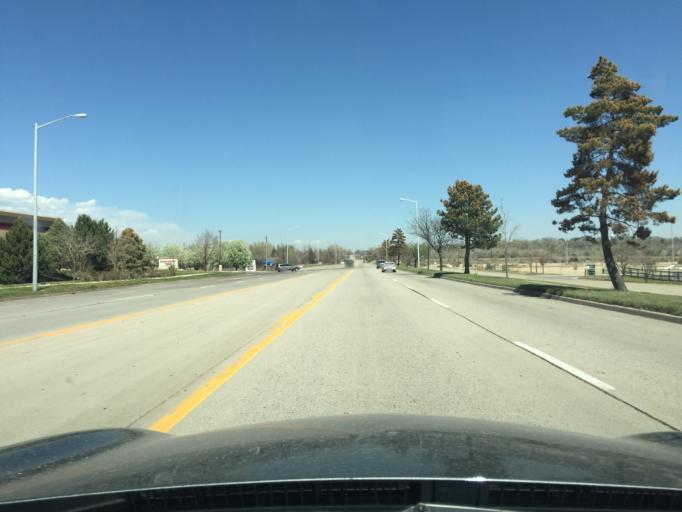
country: US
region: Colorado
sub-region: Boulder County
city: Longmont
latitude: 40.1549
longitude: -105.1306
